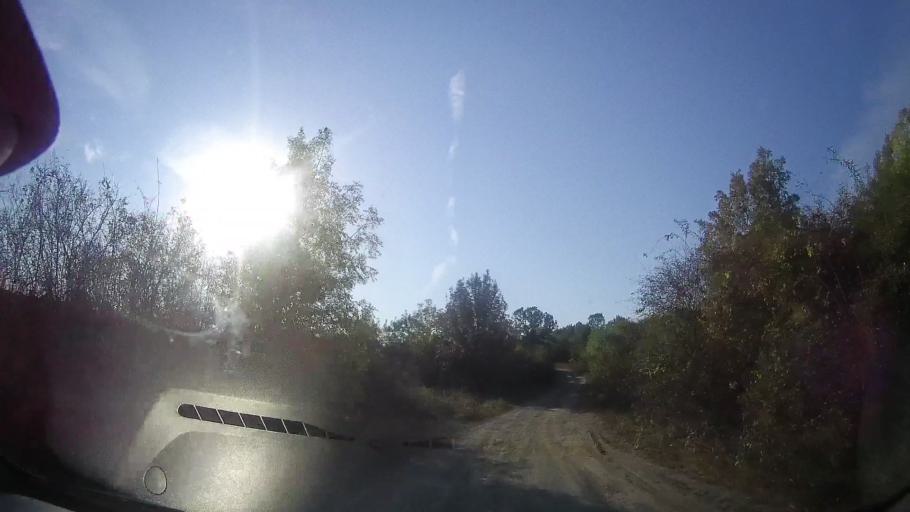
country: RO
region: Timis
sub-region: Comuna Bogda
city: Bogda
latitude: 45.9504
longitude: 21.6173
